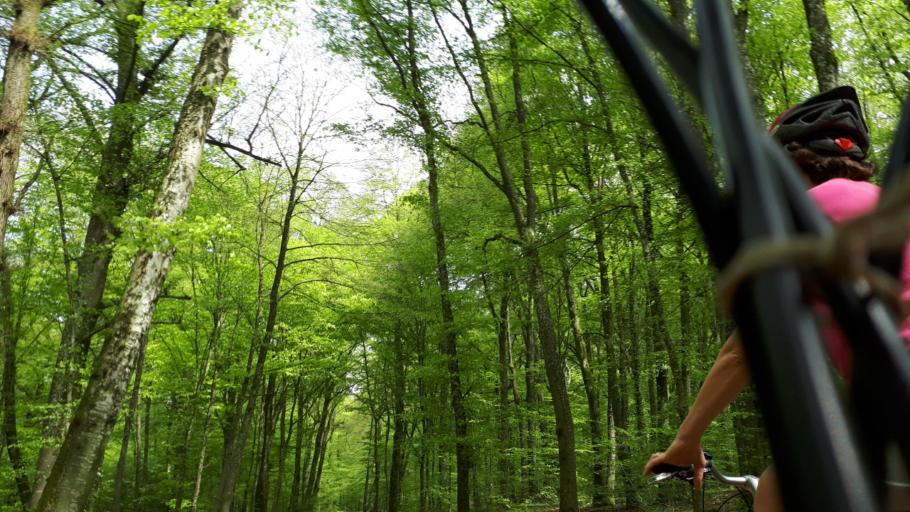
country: LU
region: Luxembourg
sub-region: Canton d'Esch-sur-Alzette
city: Leudelange
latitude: 49.5915
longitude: 6.0694
